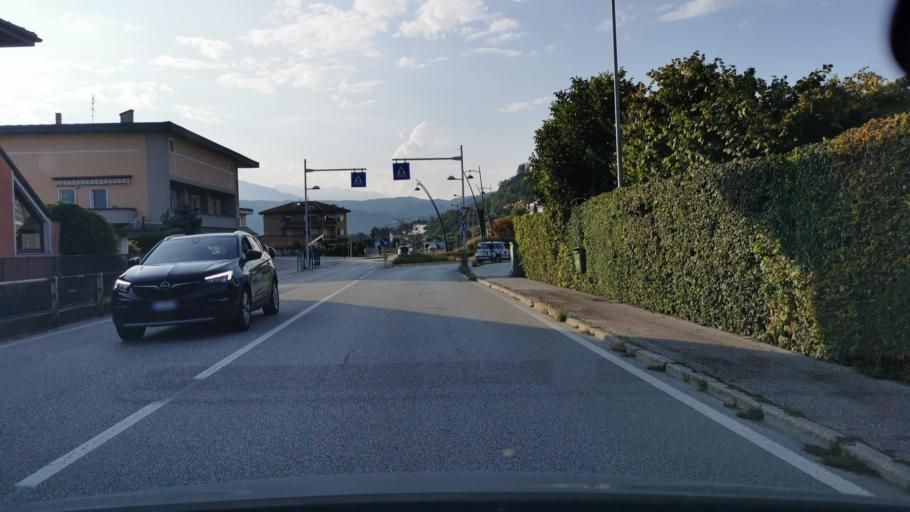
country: IT
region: Trentino-Alto Adige
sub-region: Provincia di Trento
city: Pergine Valsugana
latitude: 46.0667
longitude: 11.2271
